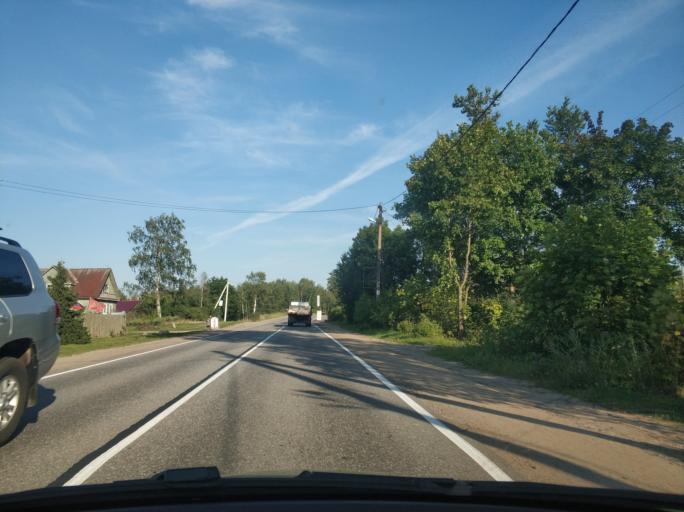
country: RU
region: Leningrad
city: Borisova Griva
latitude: 60.0915
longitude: 31.0151
